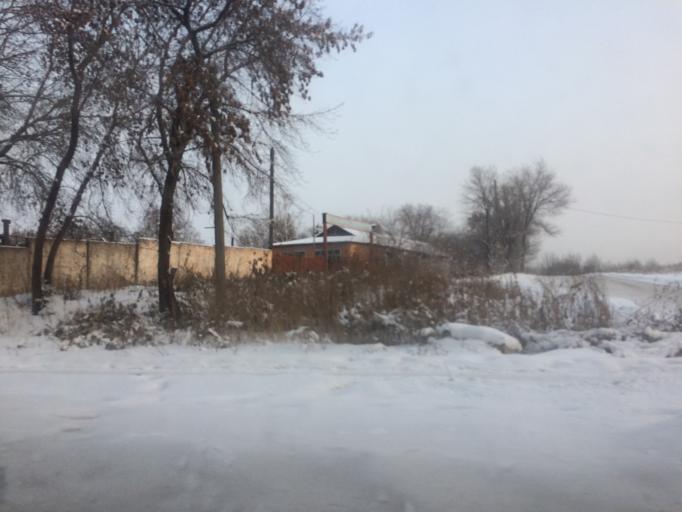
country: RU
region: Chelyabinsk
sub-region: Gorod Magnitogorsk
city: Magnitogorsk
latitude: 53.4675
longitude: 59.0738
